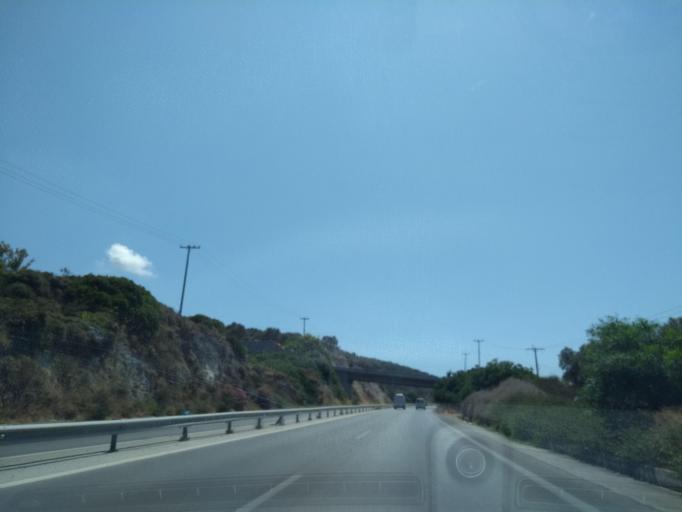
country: GR
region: Crete
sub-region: Nomos Rethymnis
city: Rethymno
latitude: 35.3618
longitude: 24.4965
